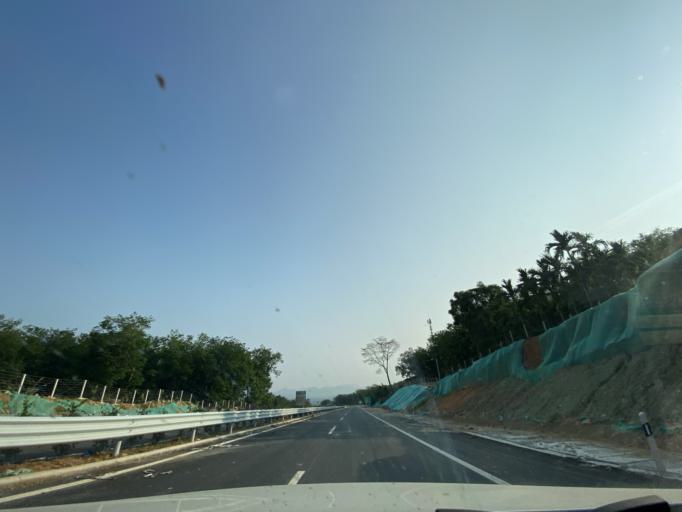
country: CN
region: Hainan
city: Xiangshui
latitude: 18.6456
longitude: 109.6294
